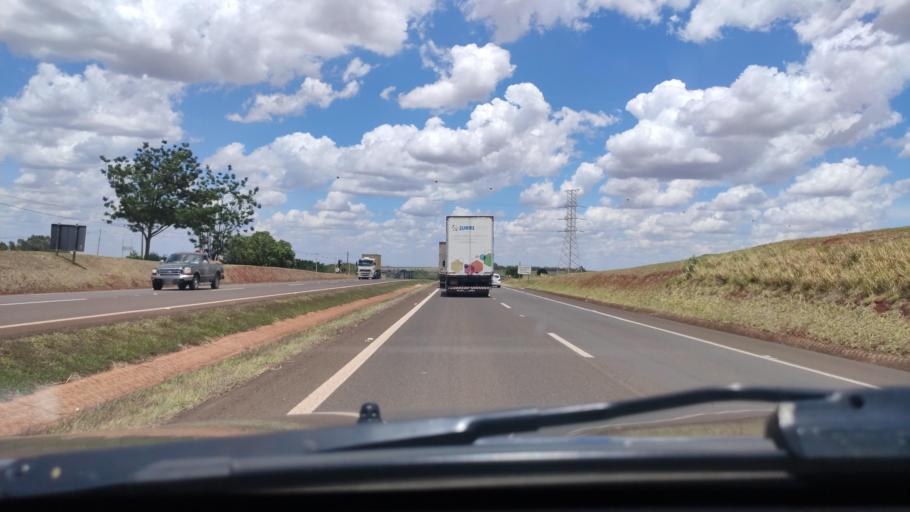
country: BR
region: Sao Paulo
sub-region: Jau
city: Jau
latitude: -22.3037
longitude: -48.5946
